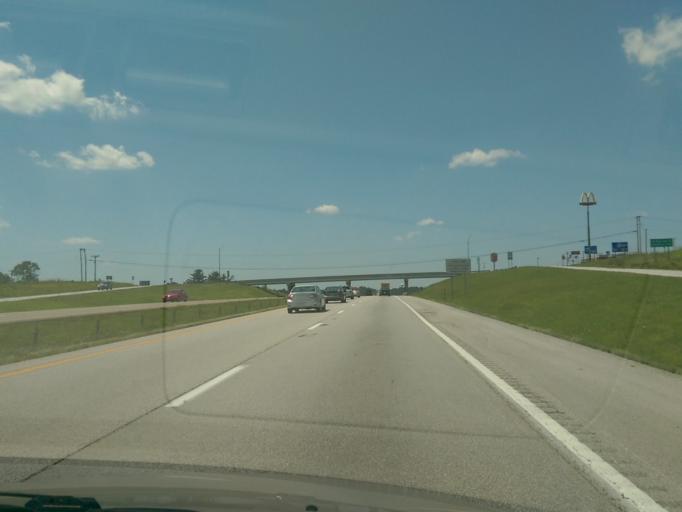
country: US
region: Missouri
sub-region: Cooper County
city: Boonville
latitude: 38.9366
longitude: -92.7413
